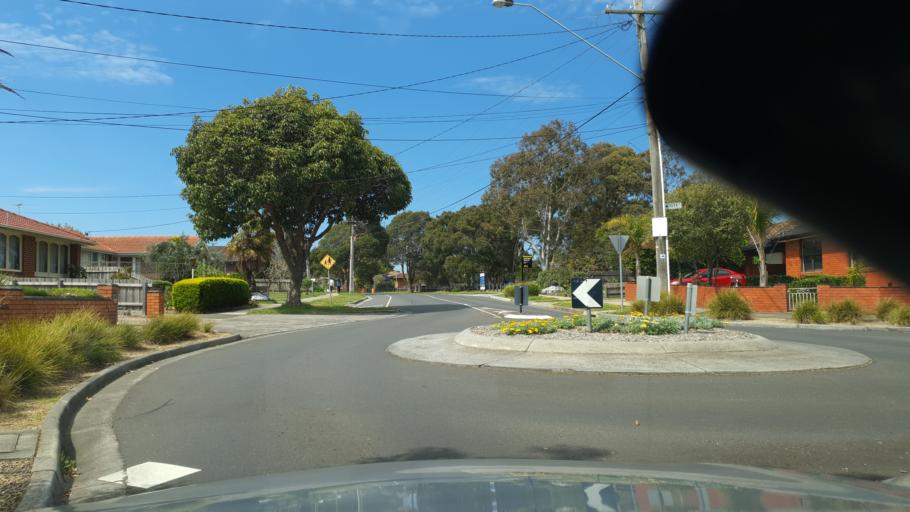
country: AU
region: Victoria
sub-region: Greater Dandenong
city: Springvale
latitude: -37.9259
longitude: 145.1614
